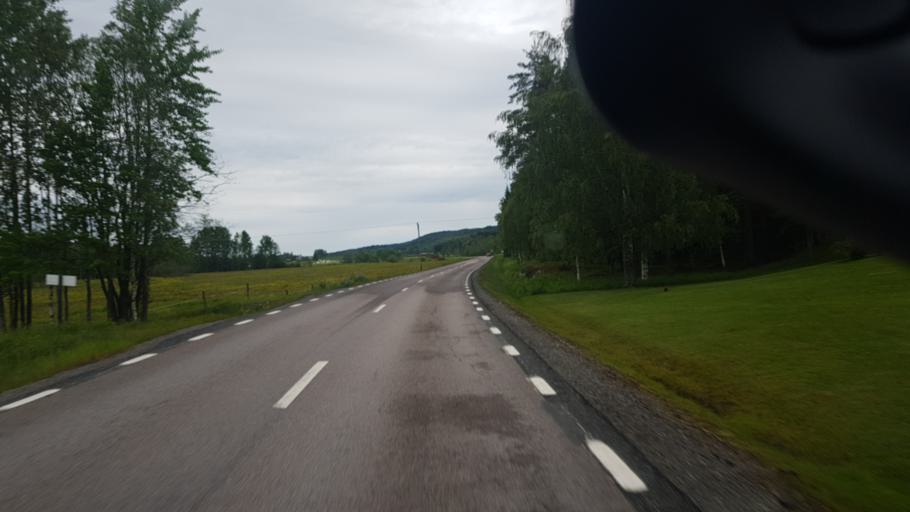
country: SE
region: Vaermland
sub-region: Arjangs Kommun
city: Arjaeng
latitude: 59.6389
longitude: 12.1368
